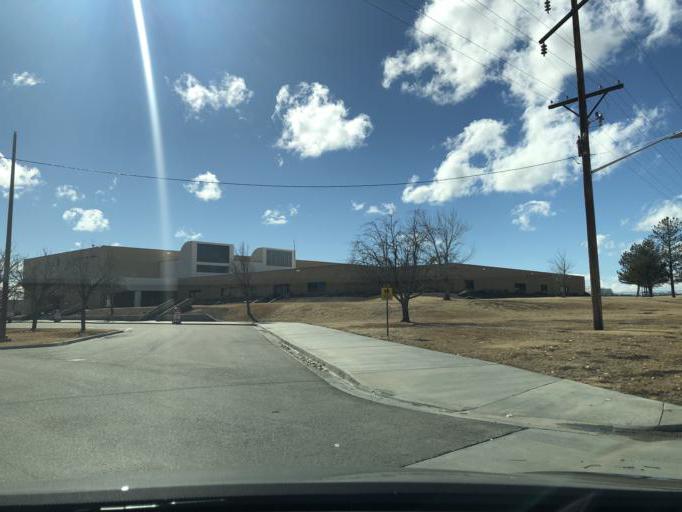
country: US
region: Utah
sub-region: Carbon County
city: East Carbon City
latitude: 39.0006
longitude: -110.1716
